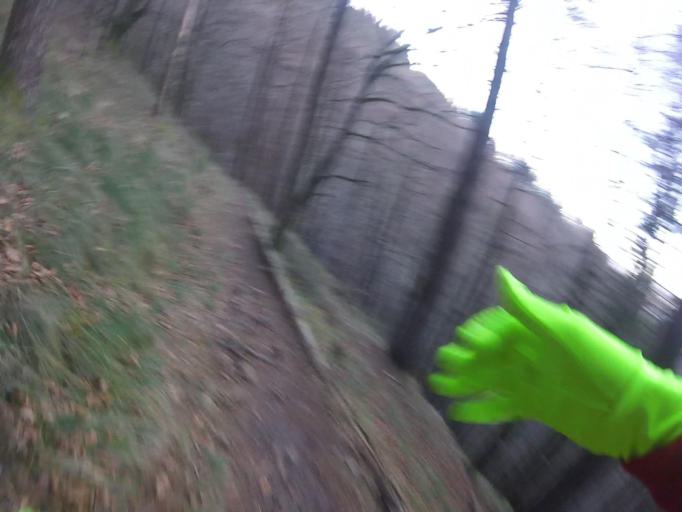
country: ES
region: Basque Country
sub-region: Provincia de Guipuzcoa
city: Irun
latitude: 43.2917
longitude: -1.7893
